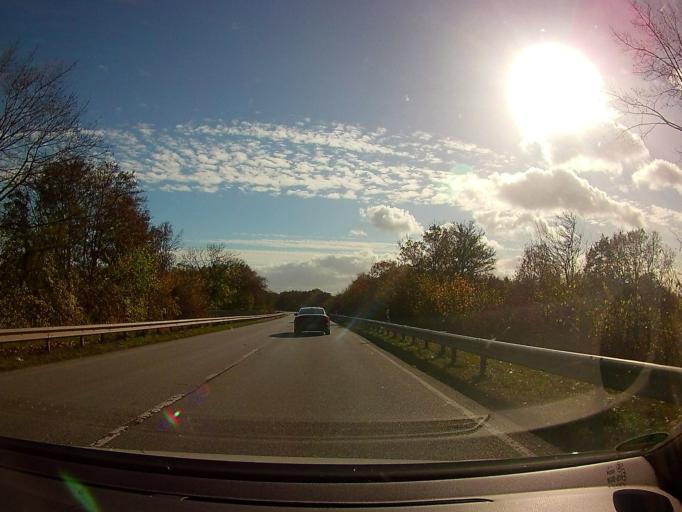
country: DE
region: Schleswig-Holstein
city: Lutjensee
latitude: 53.6660
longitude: 10.3831
